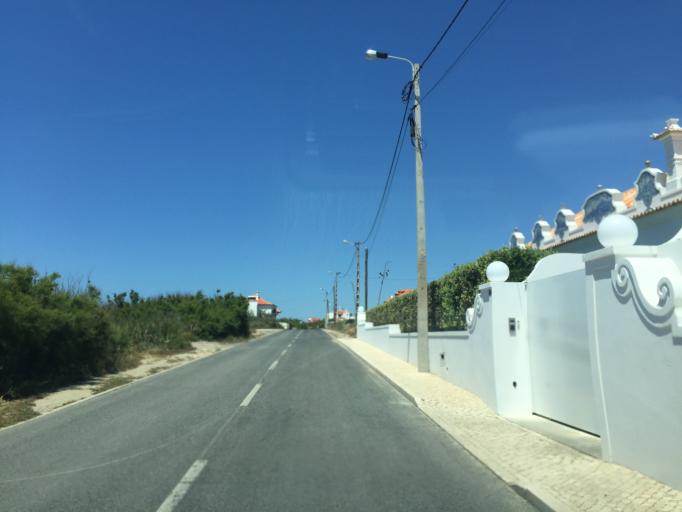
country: PT
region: Lisbon
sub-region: Sintra
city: Colares
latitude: 38.8336
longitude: -9.4667
